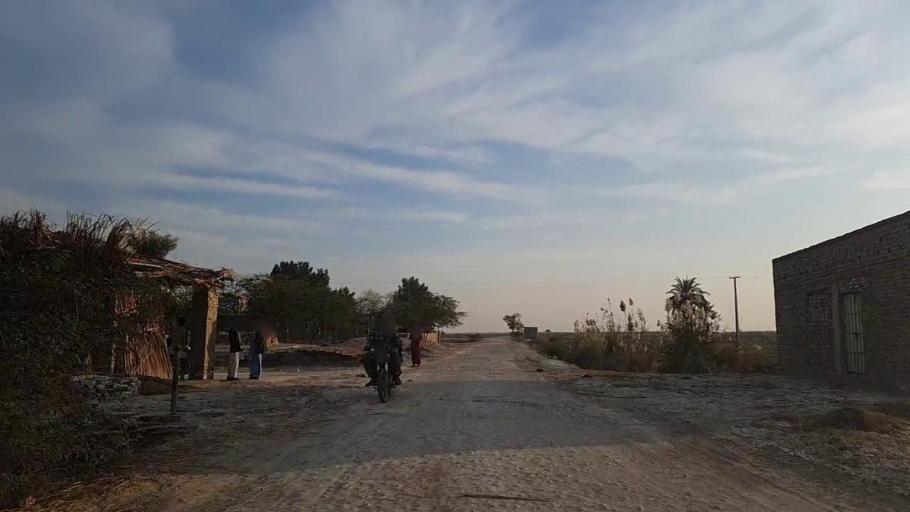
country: PK
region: Sindh
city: Bandhi
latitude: 26.5834
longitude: 68.3333
